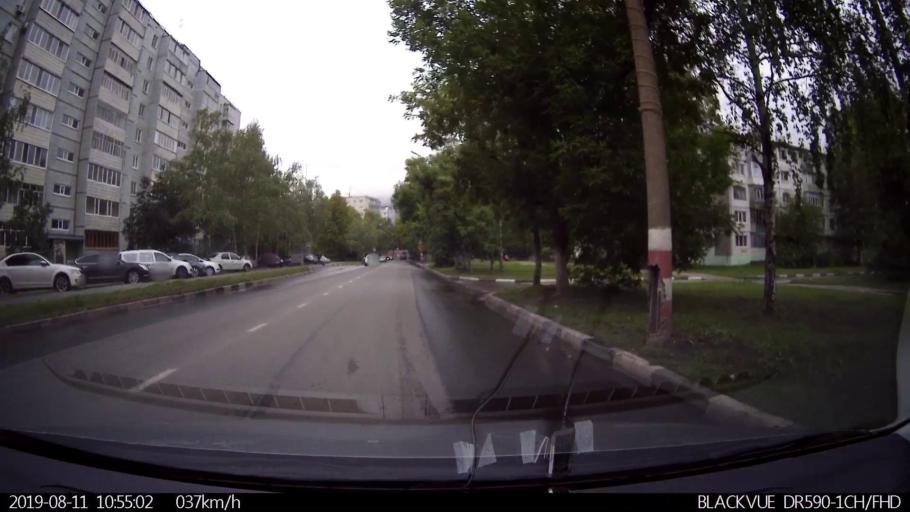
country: RU
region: Ulyanovsk
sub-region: Ulyanovskiy Rayon
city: Ulyanovsk
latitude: 54.2556
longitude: 48.3322
